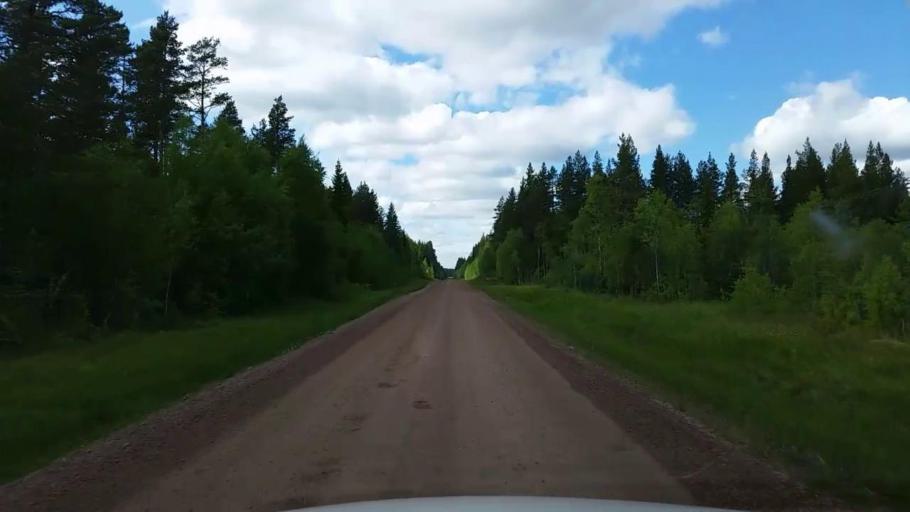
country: SE
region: Gaevleborg
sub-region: Ovanakers Kommun
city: Alfta
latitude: 61.4702
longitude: 16.0220
